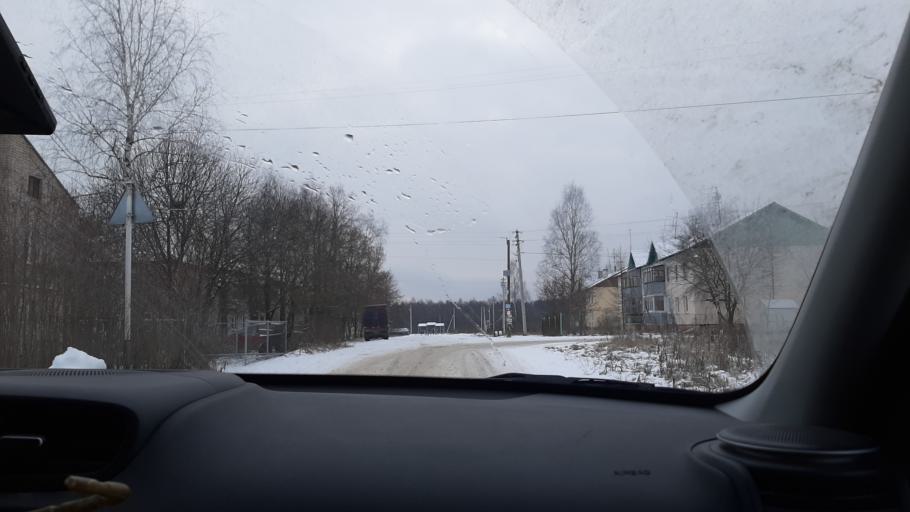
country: RU
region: Ivanovo
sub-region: Gorod Ivanovo
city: Ivanovo
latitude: 56.9266
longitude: 40.9828
